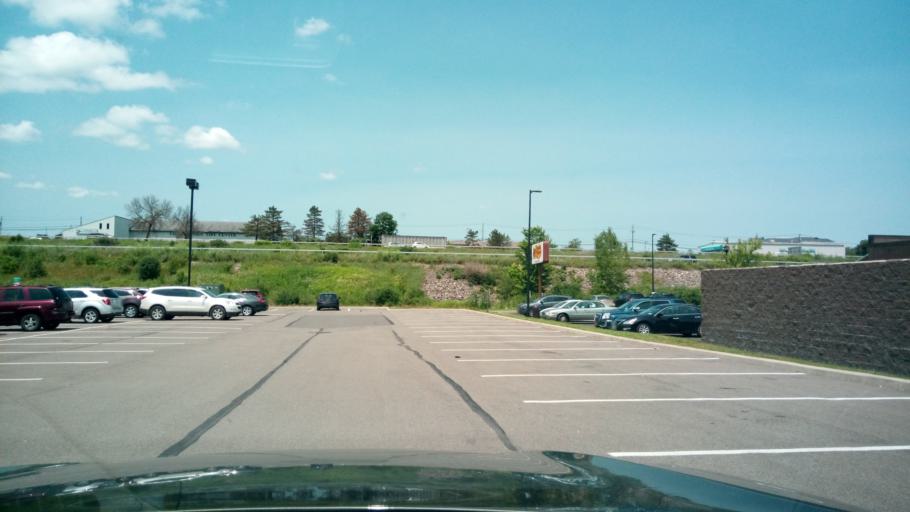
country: US
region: New York
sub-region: Chemung County
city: Horseheads
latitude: 42.1592
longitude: -76.8578
